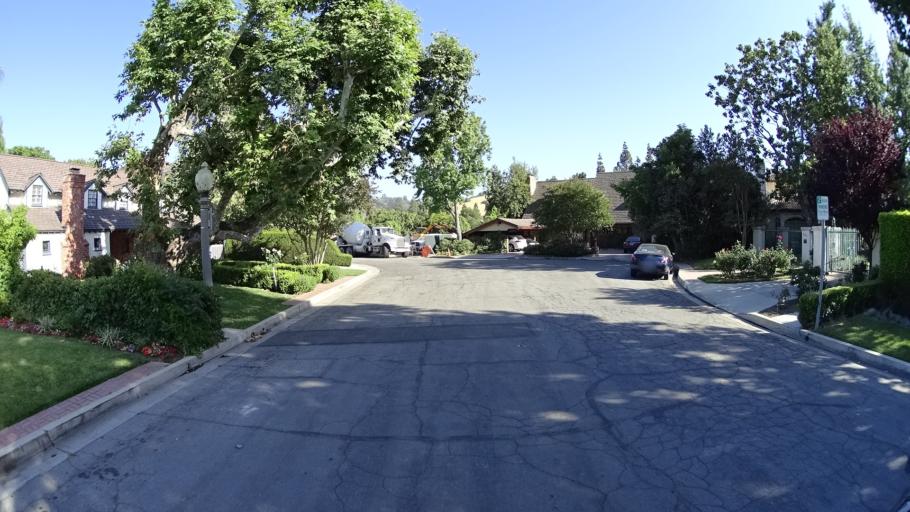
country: US
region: California
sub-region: Los Angeles County
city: Universal City
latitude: 34.1465
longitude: -118.3455
